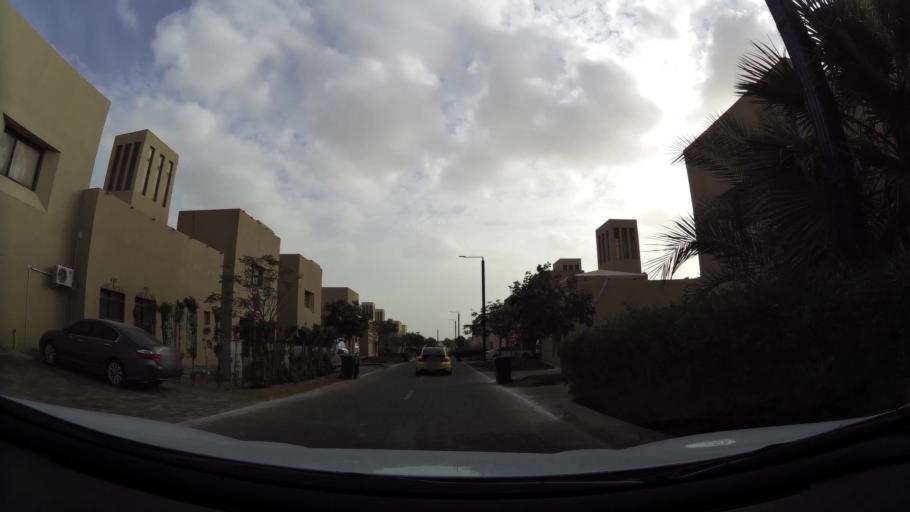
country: AE
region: Abu Dhabi
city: Abu Dhabi
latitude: 24.5025
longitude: 54.5946
